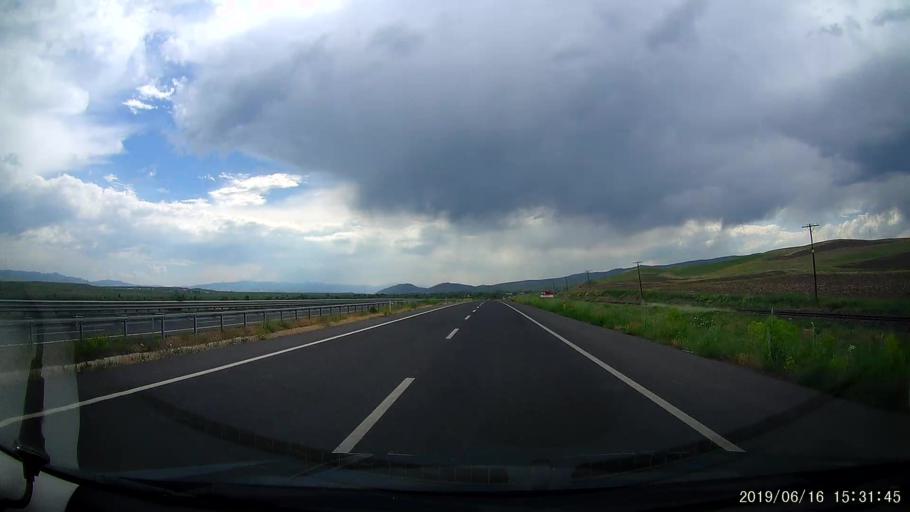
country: TR
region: Erzurum
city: Horasan
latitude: 40.0311
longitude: 42.0695
